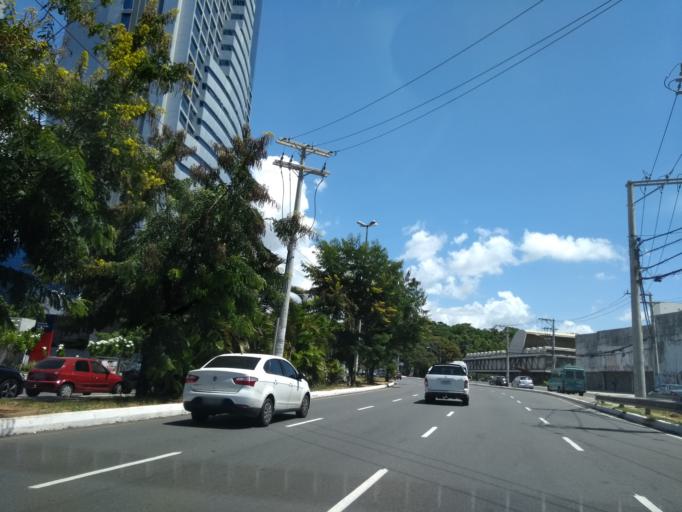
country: BR
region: Bahia
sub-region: Salvador
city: Salvador
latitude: -12.9816
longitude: -38.4503
